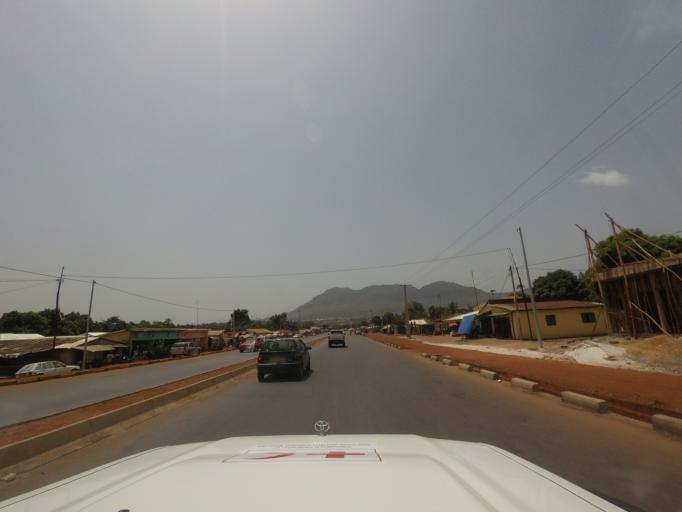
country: GN
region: Kindia
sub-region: Coyah
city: Coyah
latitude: 9.7186
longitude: -13.4113
